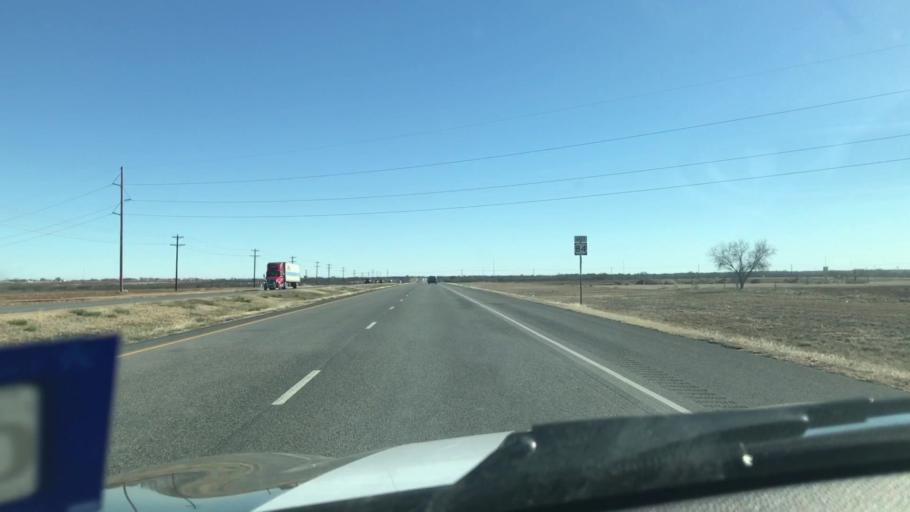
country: US
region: Texas
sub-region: Scurry County
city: Snyder
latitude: 32.7769
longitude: -100.9425
